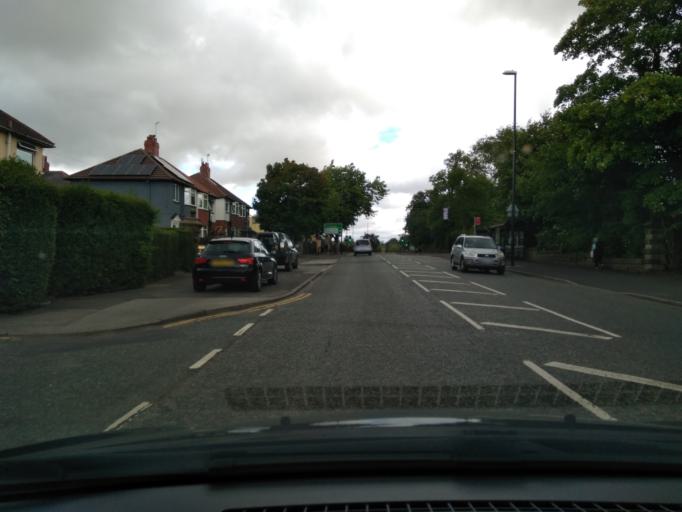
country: GB
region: England
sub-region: North Yorkshire
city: Knaresborough
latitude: 54.0019
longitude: -1.4958
